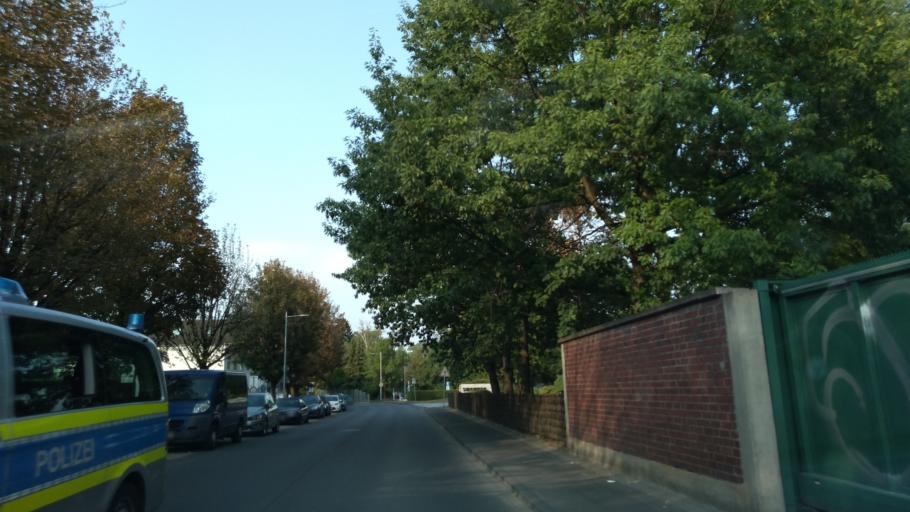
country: DE
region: North Rhine-Westphalia
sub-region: Regierungsbezirk Koln
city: Siegburg
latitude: 50.7953
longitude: 7.2139
